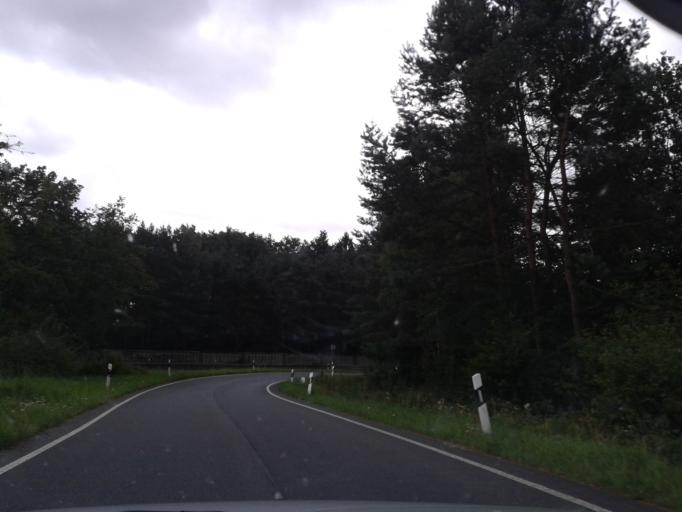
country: DE
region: North Rhine-Westphalia
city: Bad Lippspringe
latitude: 51.8011
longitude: 8.8059
